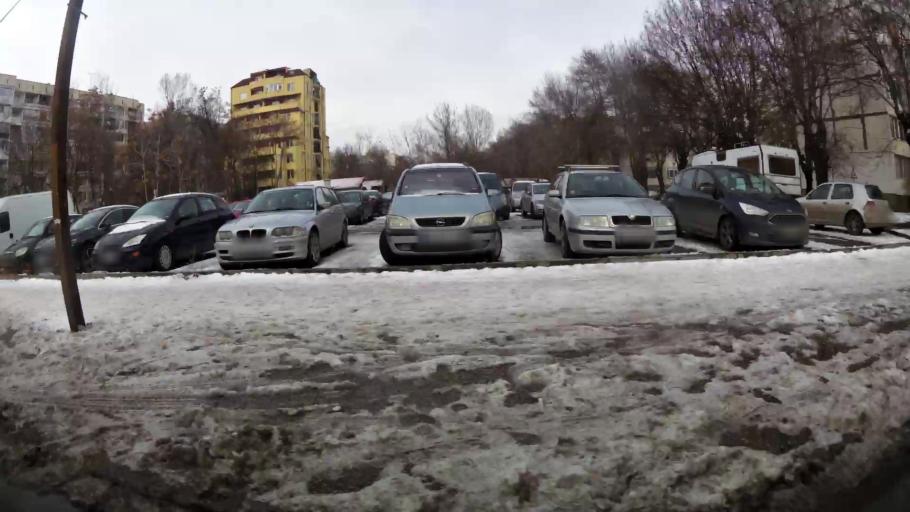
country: BG
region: Sofia-Capital
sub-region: Stolichna Obshtina
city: Sofia
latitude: 42.7066
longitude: 23.3487
